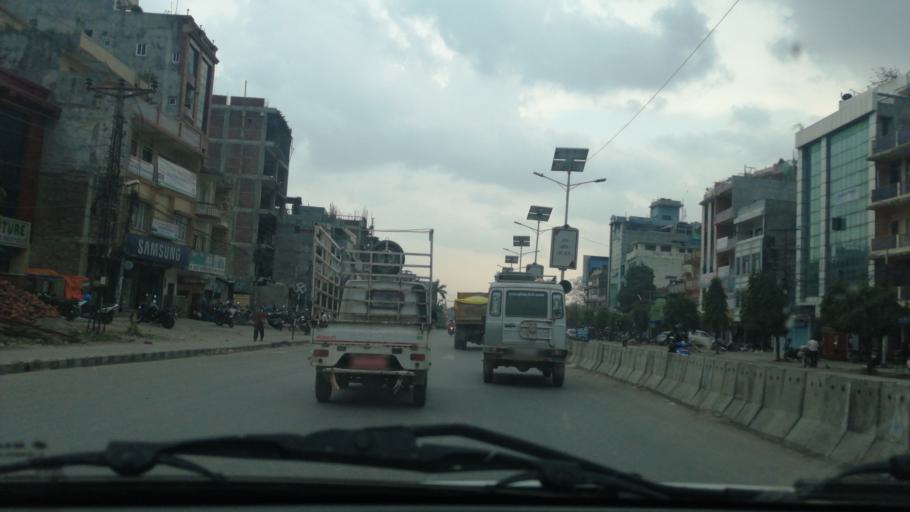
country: NP
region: Western Region
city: Butwal
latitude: 27.7002
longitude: 83.4659
